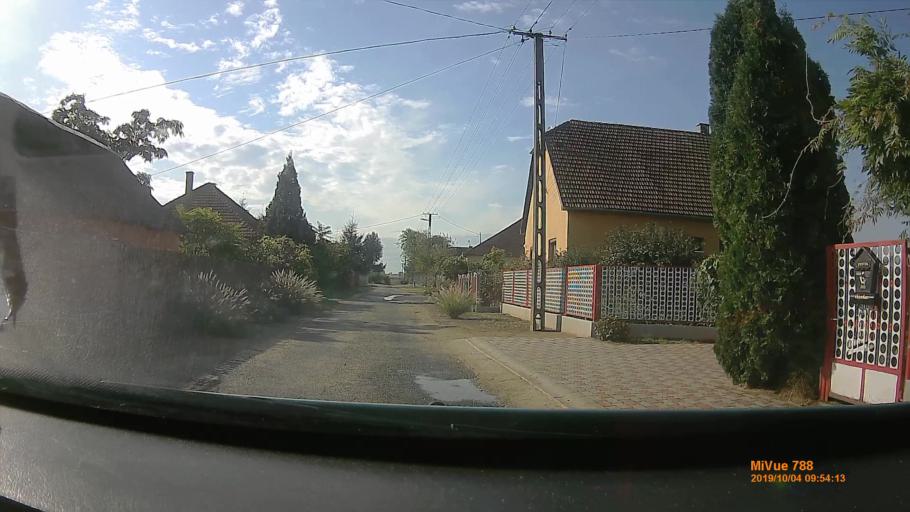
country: HU
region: Szabolcs-Szatmar-Bereg
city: Nyiregyhaza
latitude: 47.9412
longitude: 21.6635
